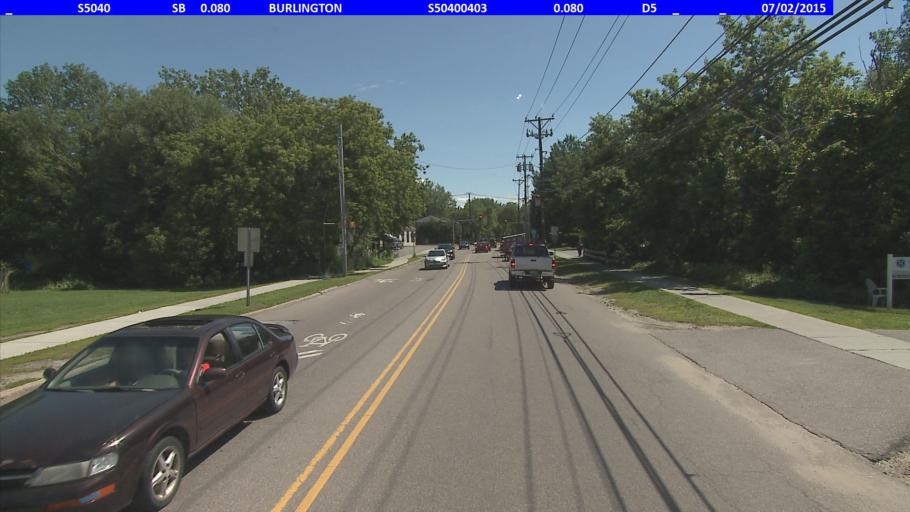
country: US
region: Vermont
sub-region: Chittenden County
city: Burlington
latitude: 44.4566
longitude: -73.2143
